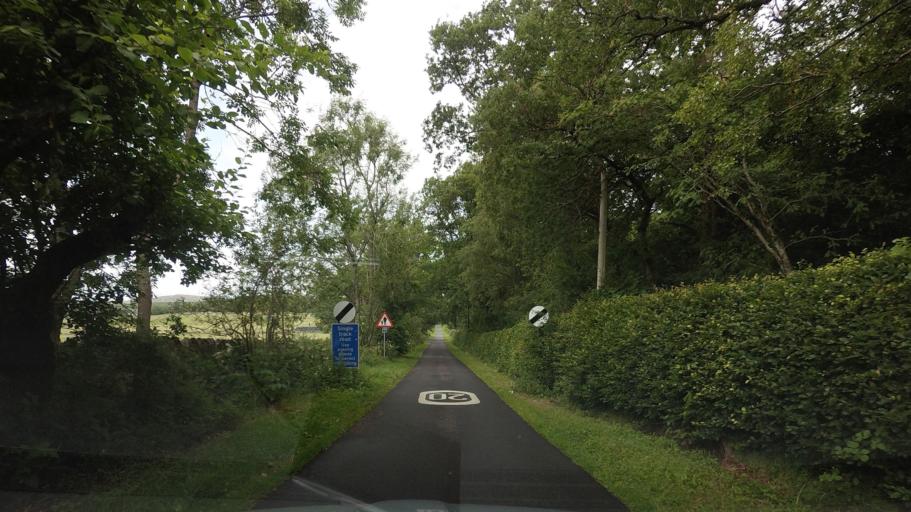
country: GB
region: Scotland
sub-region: Stirling
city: Killearn
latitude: 56.0702
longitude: -4.4511
